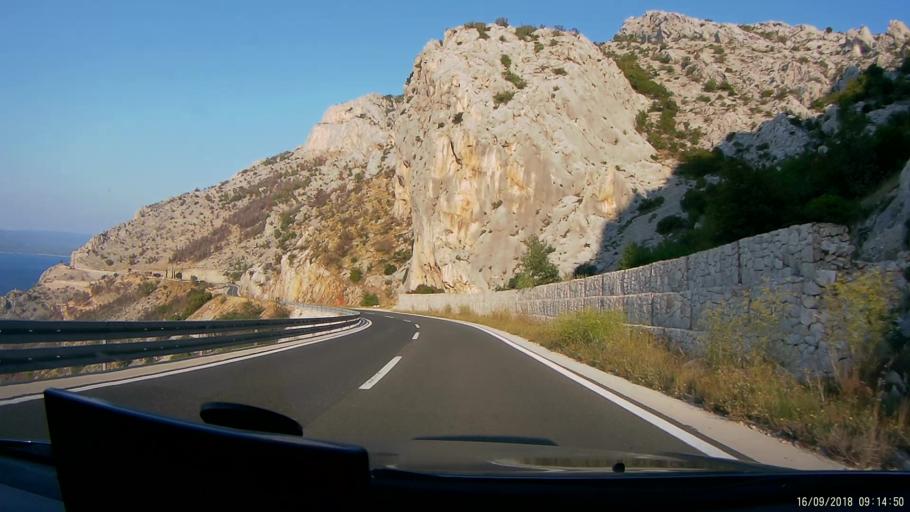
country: HR
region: Splitsko-Dalmatinska
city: Donja Brela
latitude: 43.4043
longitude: 16.8856
